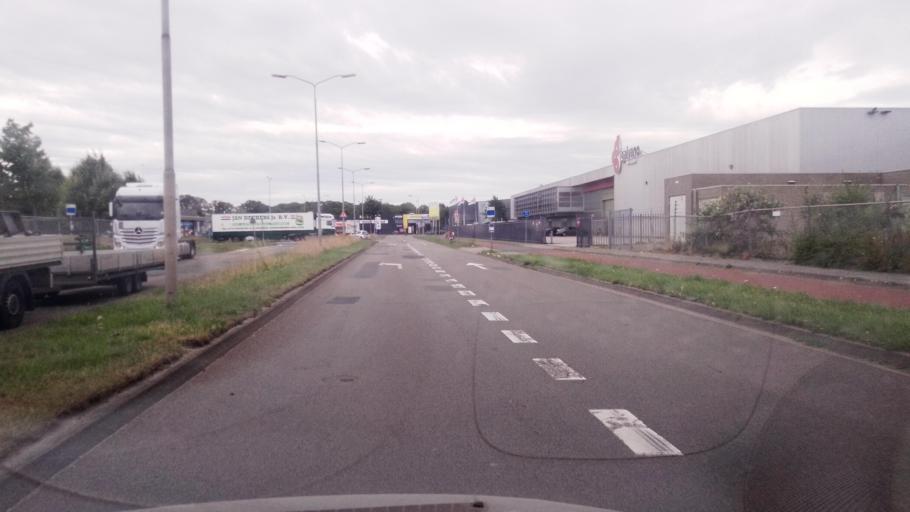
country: NL
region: North Brabant
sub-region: Gemeente Eindhoven
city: Meerhoven
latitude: 51.4675
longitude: 5.4198
